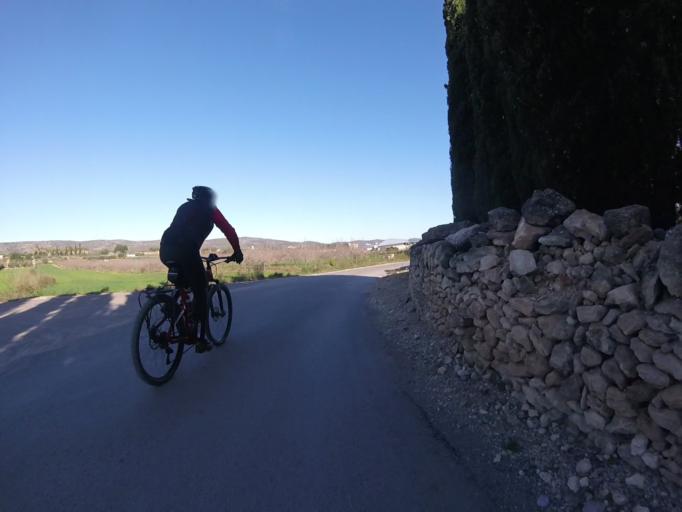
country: ES
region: Valencia
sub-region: Provincia de Castello
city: Alcala de Xivert
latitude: 40.2960
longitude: 0.2193
